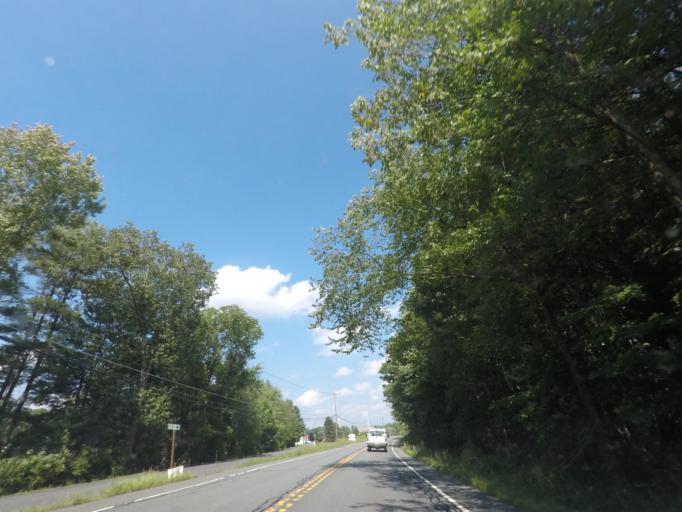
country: US
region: New York
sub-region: Rensselaer County
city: Hoosick Falls
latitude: 42.8317
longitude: -73.4887
